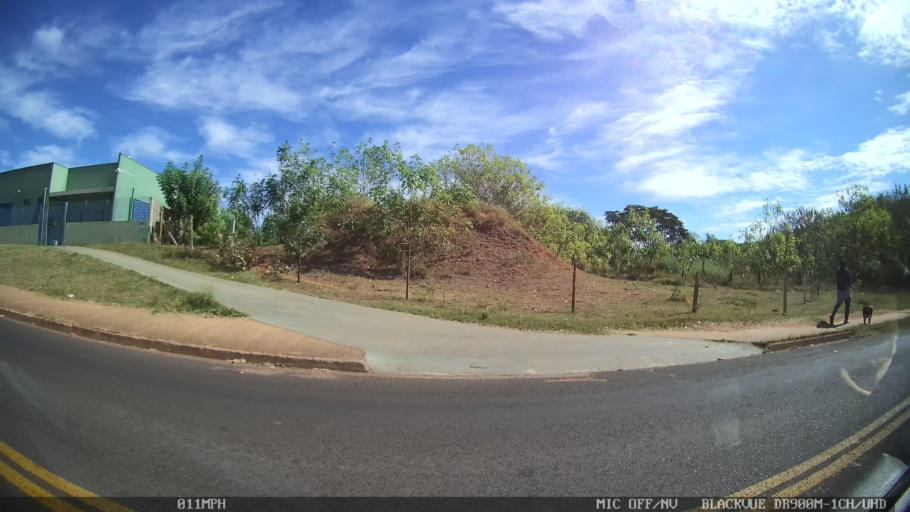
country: BR
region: Sao Paulo
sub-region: Bady Bassitt
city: Bady Bassitt
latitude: -20.8265
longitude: -49.4945
